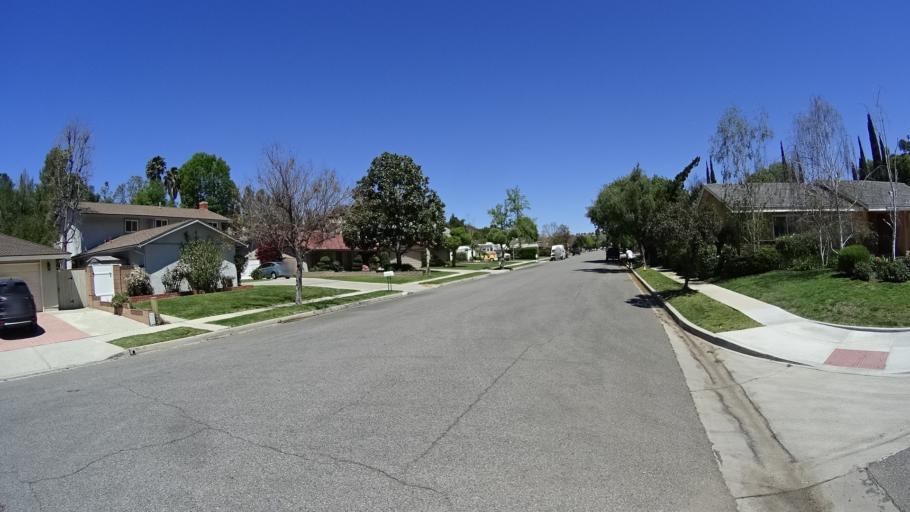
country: US
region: California
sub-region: Ventura County
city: Thousand Oaks
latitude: 34.1955
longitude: -118.8439
